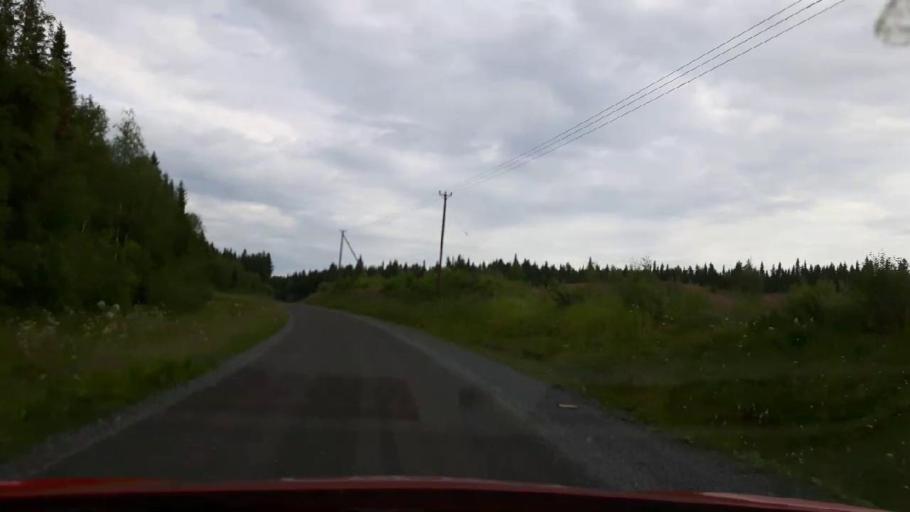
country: SE
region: Jaemtland
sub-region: Stroemsunds Kommun
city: Stroemsund
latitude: 63.4785
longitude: 15.3010
